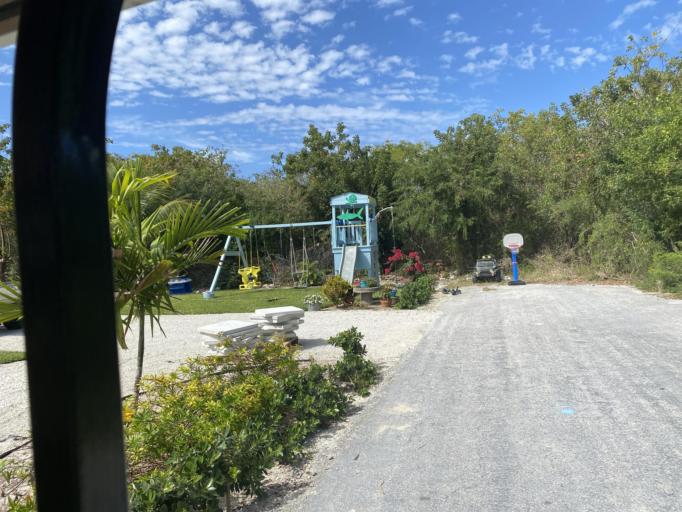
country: BS
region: Spanish Wells
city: Spanish Wells
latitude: 25.5454
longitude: -76.7784
